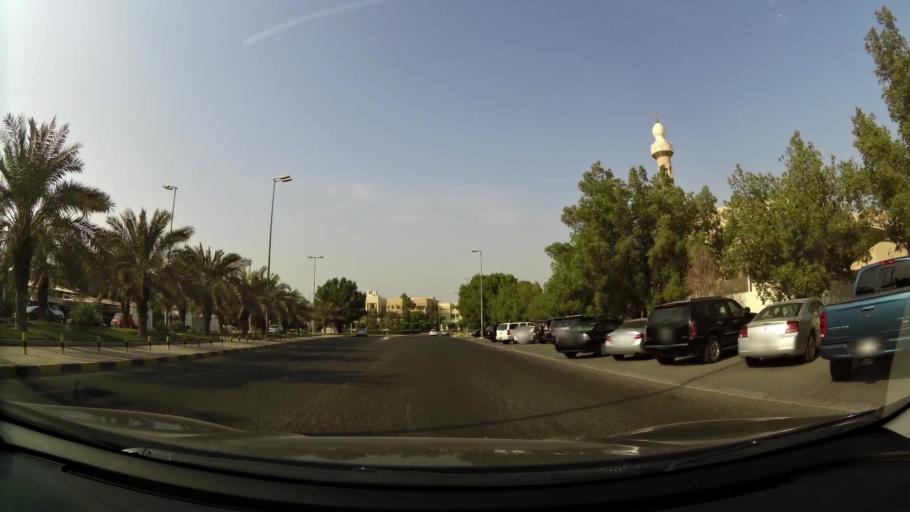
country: KW
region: Al Asimah
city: Ash Shamiyah
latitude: 29.3317
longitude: 47.9805
